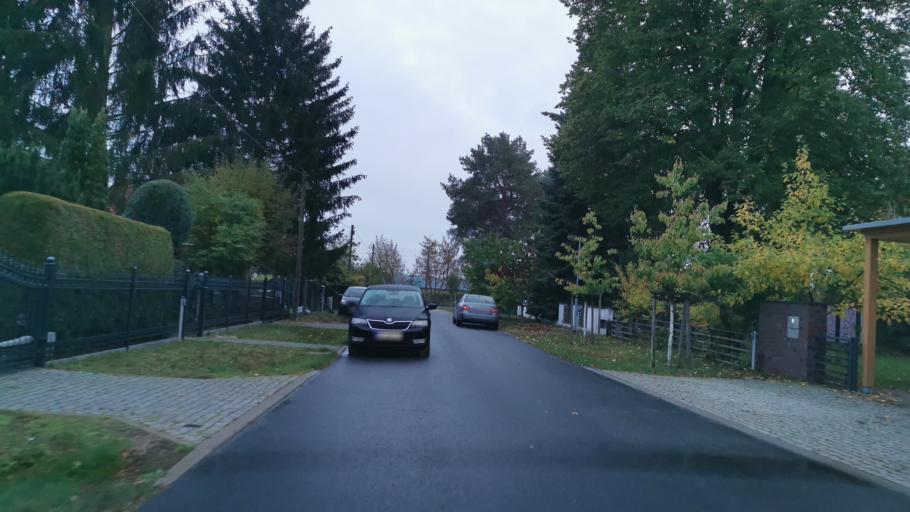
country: DE
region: Brandenburg
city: Michendorf
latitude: 52.3249
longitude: 13.0690
